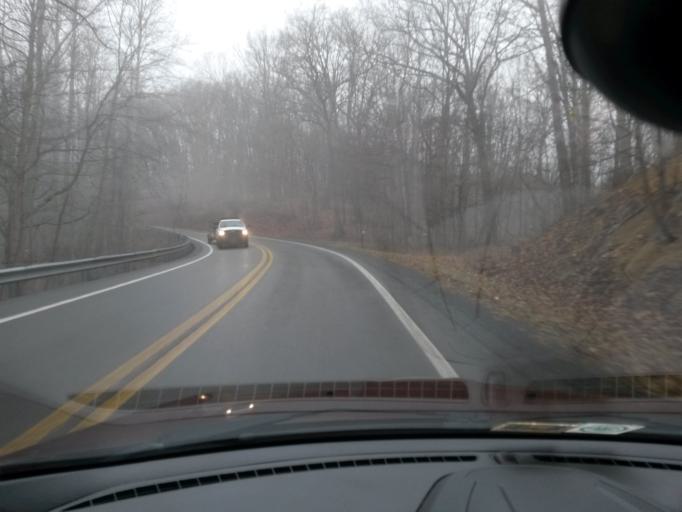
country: US
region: West Virginia
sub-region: Greenbrier County
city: Lewisburg
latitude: 37.8696
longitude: -80.5396
